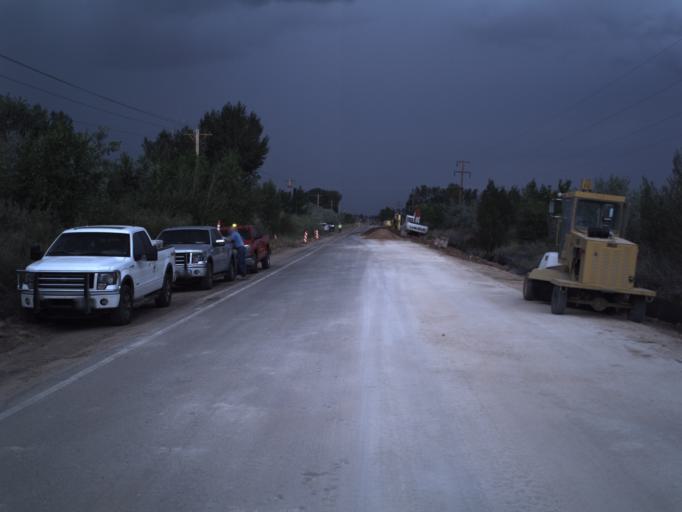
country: US
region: Utah
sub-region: Duchesne County
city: Roosevelt
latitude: 40.3915
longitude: -110.0298
